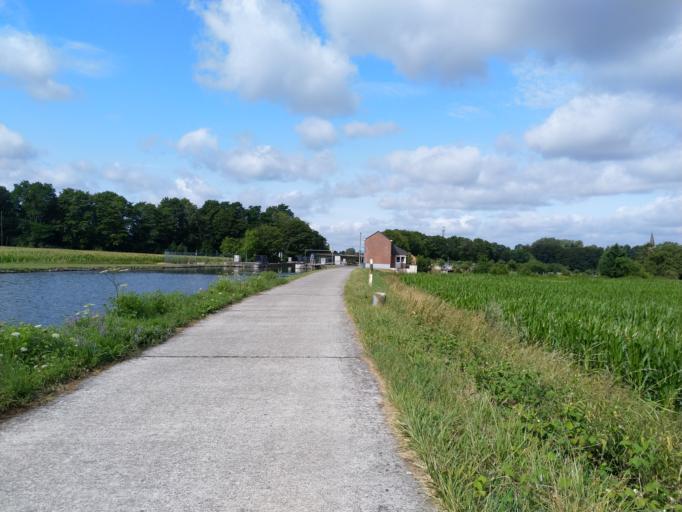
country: BE
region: Wallonia
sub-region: Province du Hainaut
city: Beloeil
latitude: 50.5030
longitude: 3.7040
